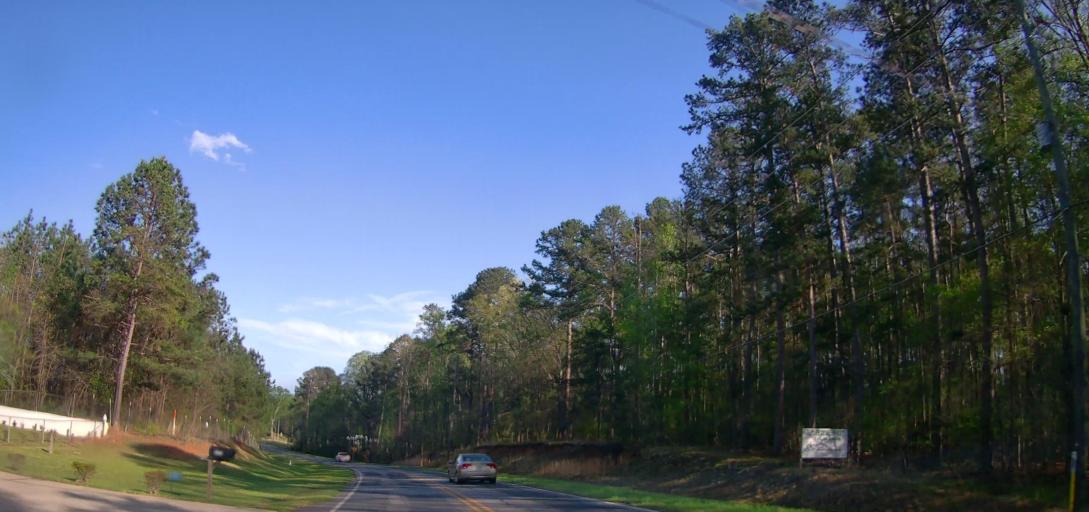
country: US
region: Georgia
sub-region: Baldwin County
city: Milledgeville
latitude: 33.1345
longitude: -83.2339
